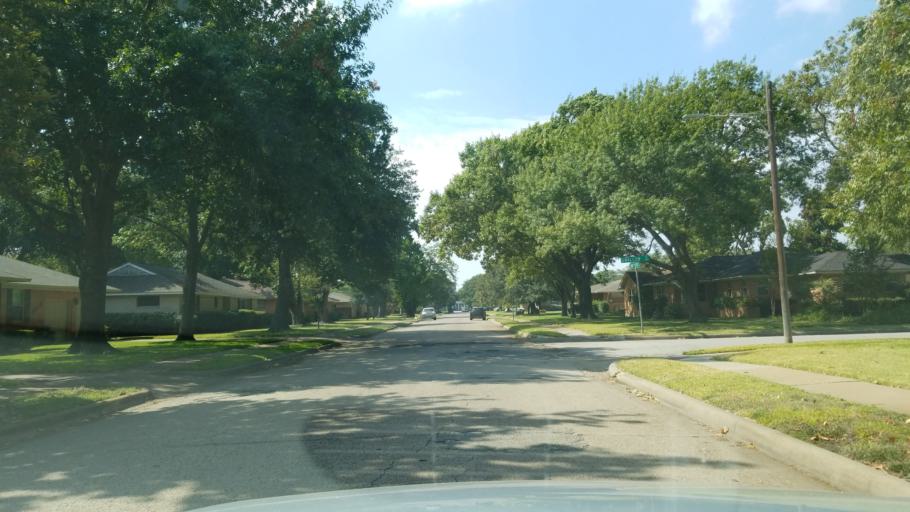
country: US
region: Texas
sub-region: Dallas County
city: Garland
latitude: 32.8996
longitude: -96.6609
